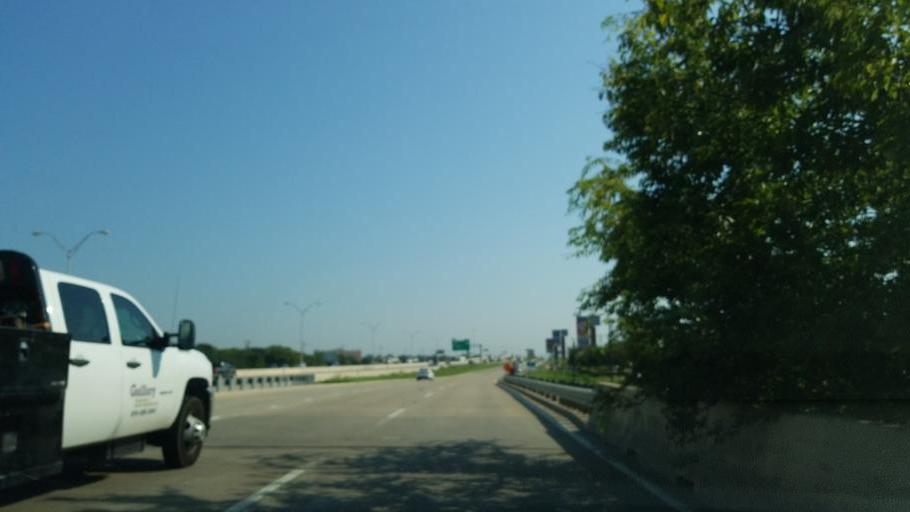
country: US
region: Texas
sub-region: Collin County
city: Allen
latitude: 33.1218
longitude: -96.6666
